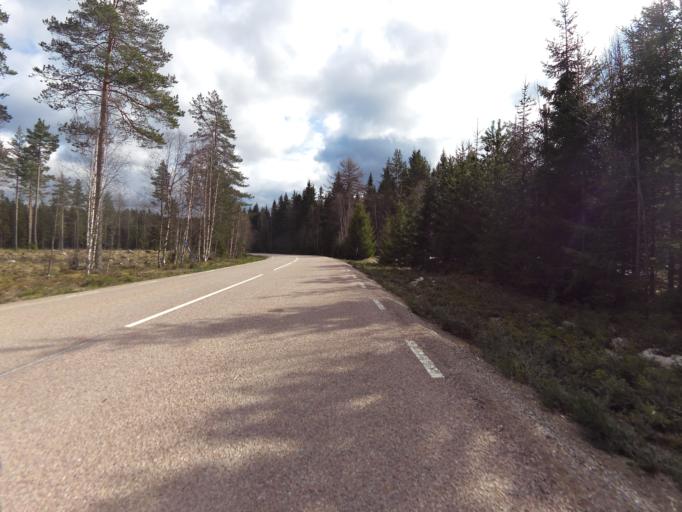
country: SE
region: Dalarna
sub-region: Avesta Kommun
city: Horndal
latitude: 60.2974
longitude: 16.2734
